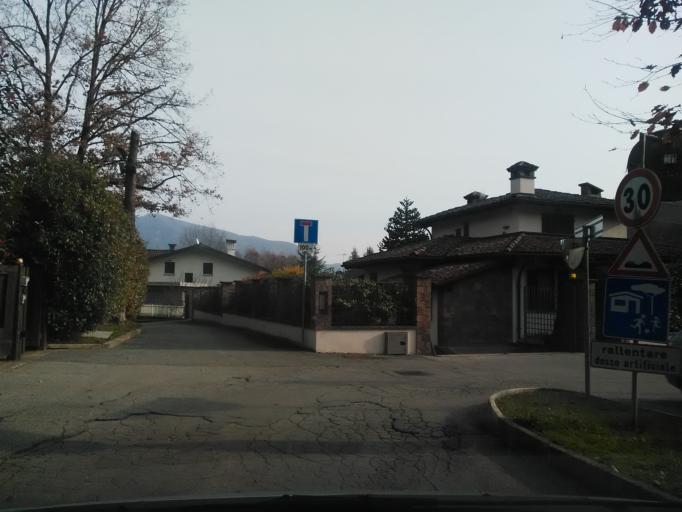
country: IT
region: Piedmont
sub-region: Provincia di Vercelli
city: Guardabosone
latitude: 45.6958
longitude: 8.2646
